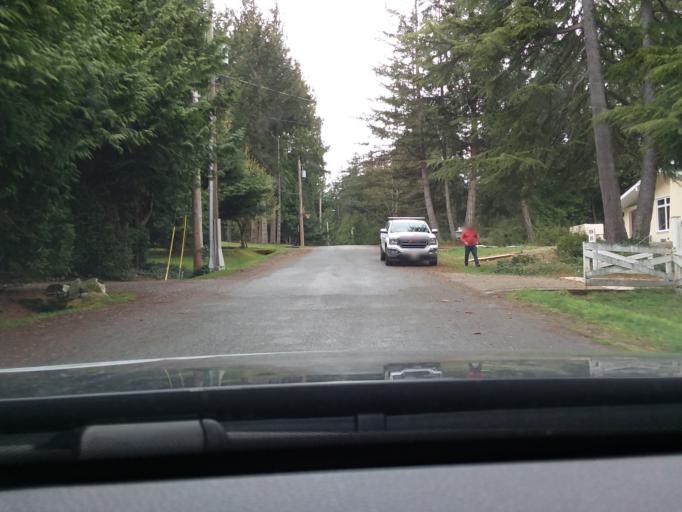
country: CA
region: British Columbia
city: North Saanich
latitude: 48.6164
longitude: -123.4191
